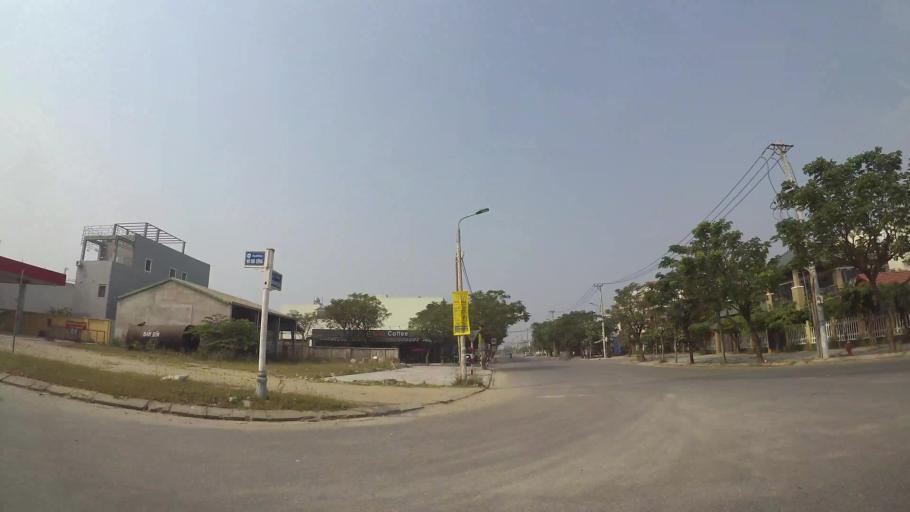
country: VN
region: Da Nang
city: Cam Le
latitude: 16.0058
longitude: 108.2211
